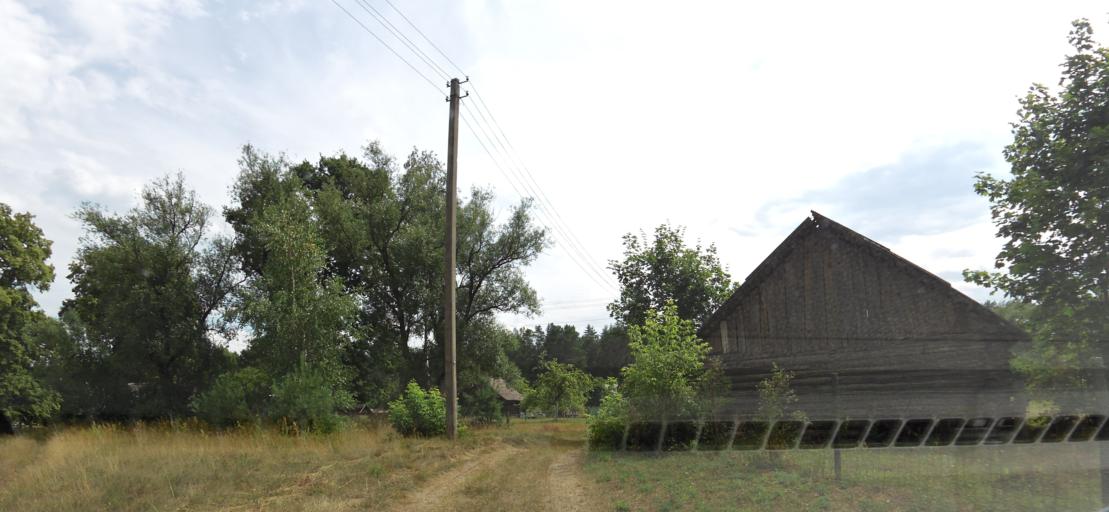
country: LT
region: Alytaus apskritis
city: Druskininkai
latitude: 53.9991
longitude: 24.2908
